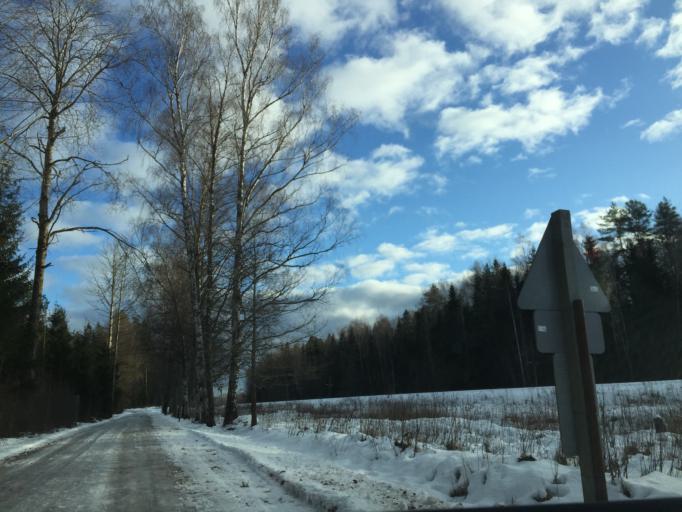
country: LV
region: Lielvarde
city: Lielvarde
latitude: 56.5743
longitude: 24.8006
